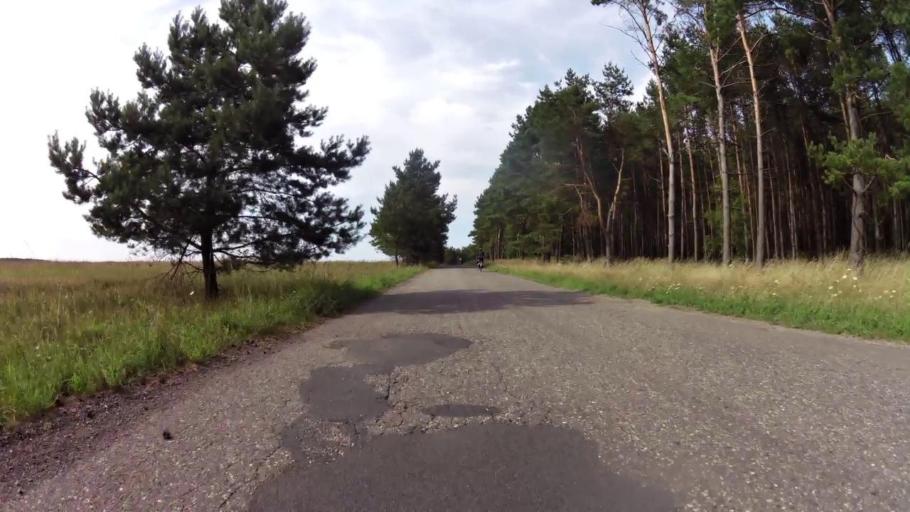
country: PL
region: West Pomeranian Voivodeship
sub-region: Powiat stargardzki
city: Insko
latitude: 53.3932
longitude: 15.5950
